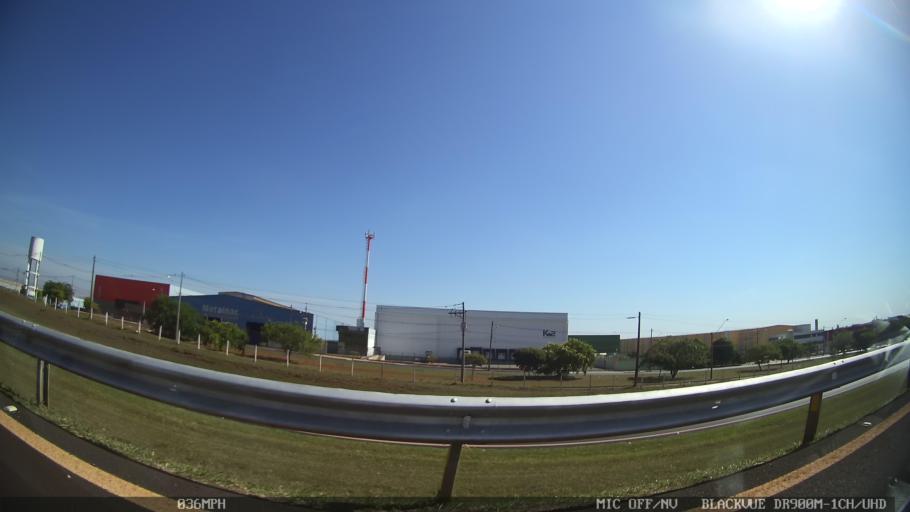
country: BR
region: Sao Paulo
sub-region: Jardinopolis
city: Jardinopolis
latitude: -21.0931
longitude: -47.7961
